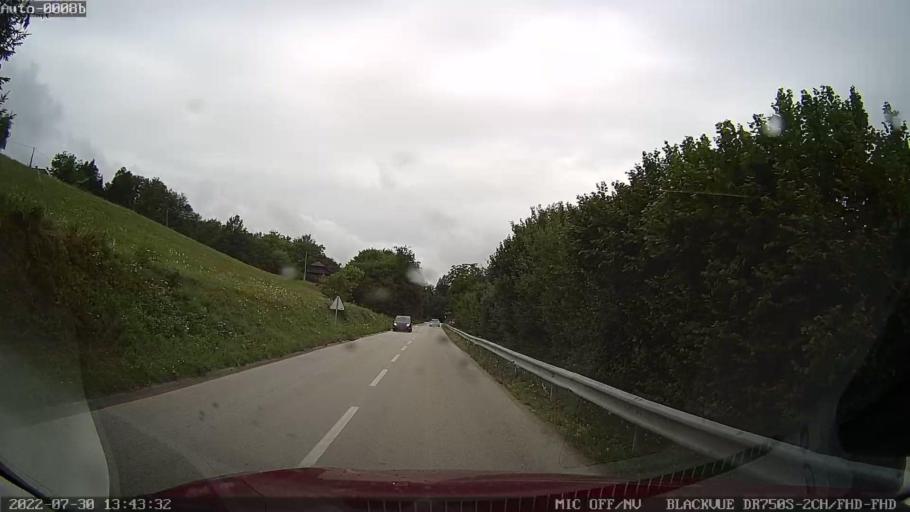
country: SI
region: Ivancna Gorica
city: Sentvid pri Sticni
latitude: 45.9130
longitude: 14.8961
